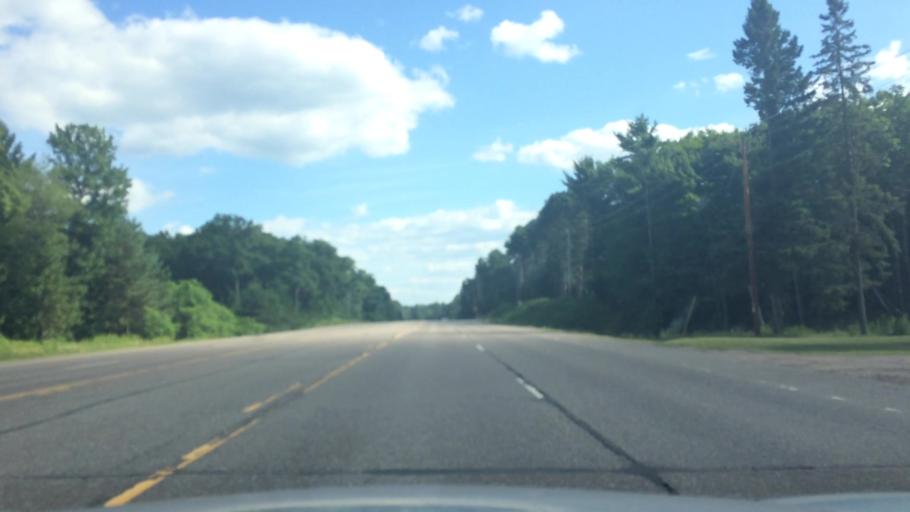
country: US
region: Wisconsin
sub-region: Vilas County
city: Lac du Flambeau
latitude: 45.8149
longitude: -89.7266
